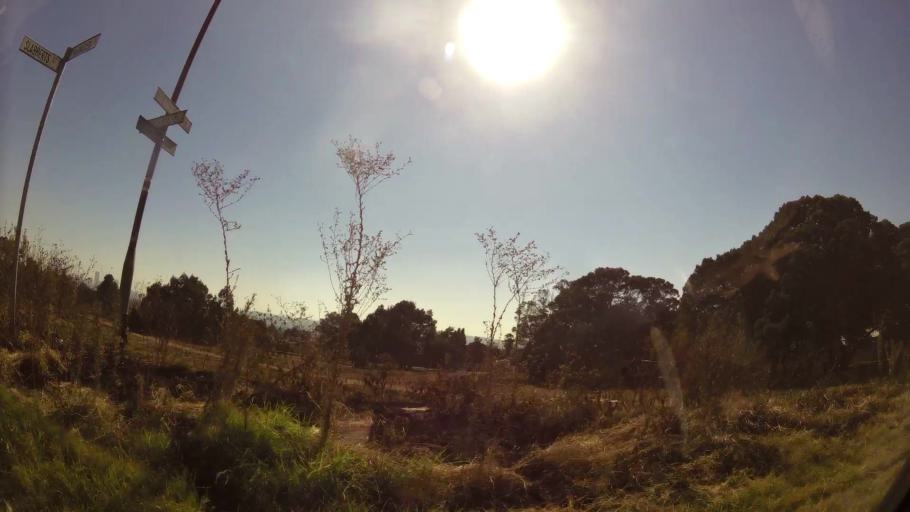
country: ZA
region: Gauteng
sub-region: City of Johannesburg Metropolitan Municipality
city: Johannesburg
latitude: -26.2451
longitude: 28.0861
